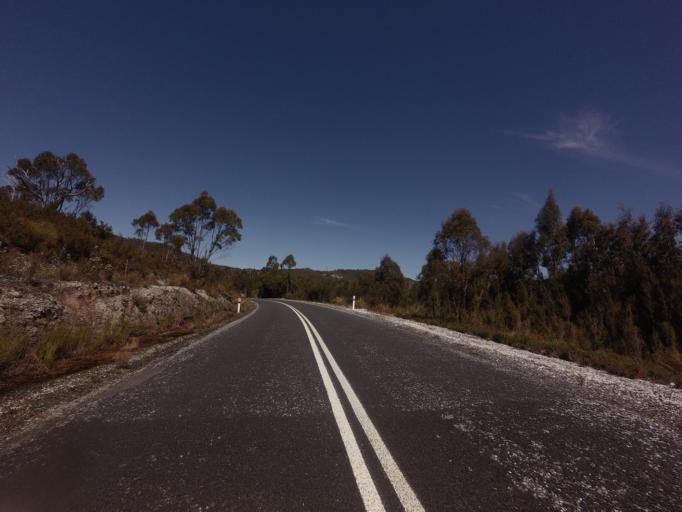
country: AU
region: Tasmania
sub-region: West Coast
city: Queenstown
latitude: -42.8002
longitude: 146.0916
